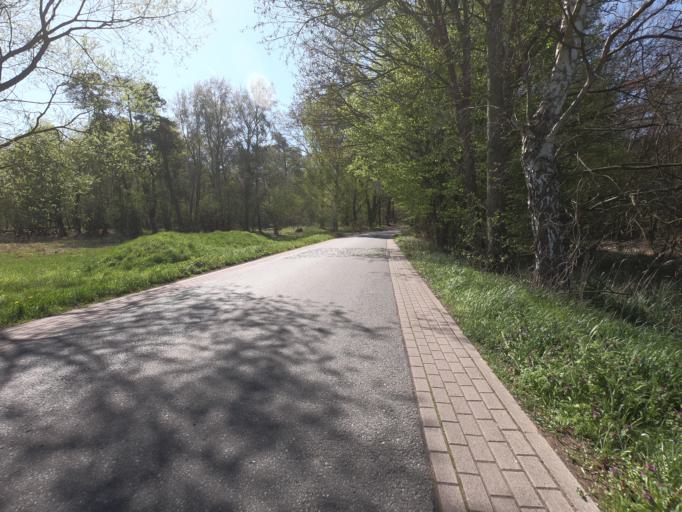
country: DE
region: Hesse
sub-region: Regierungsbezirk Darmstadt
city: Erzhausen
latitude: 49.9474
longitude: 8.6155
